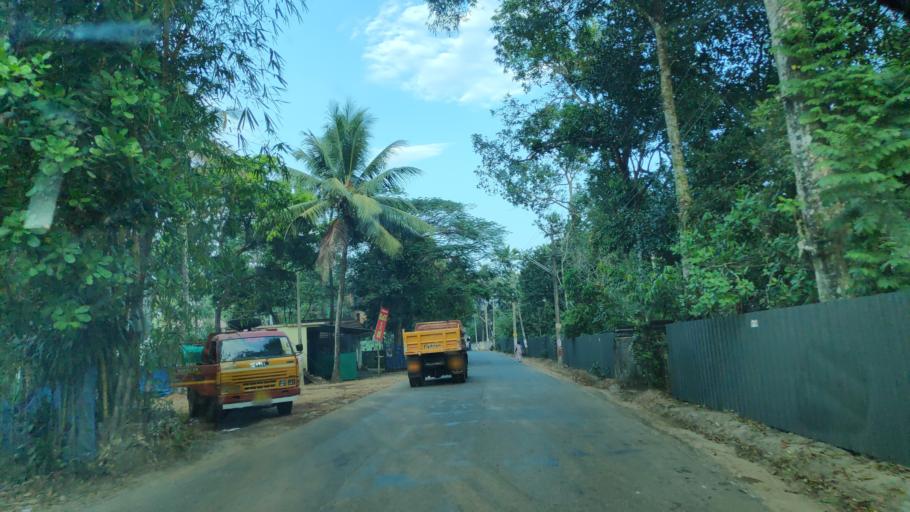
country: IN
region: Kerala
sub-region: Alappuzha
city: Shertallai
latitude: 9.6613
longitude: 76.3795
